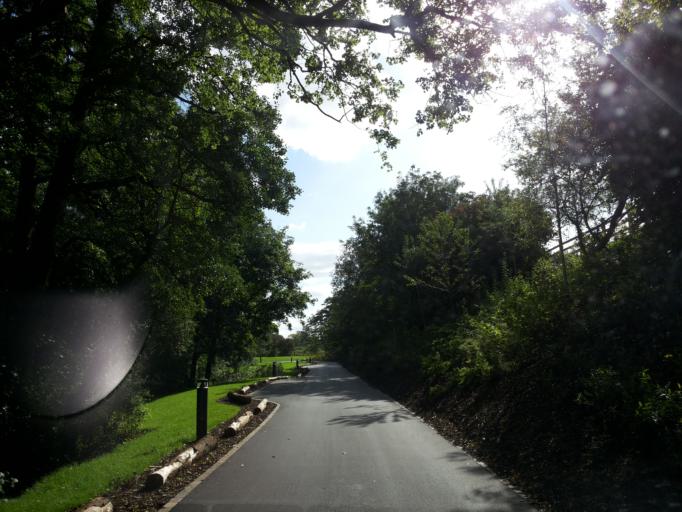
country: GB
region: England
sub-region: Bath and North East Somerset
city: Corston
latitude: 51.3801
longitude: -2.4121
